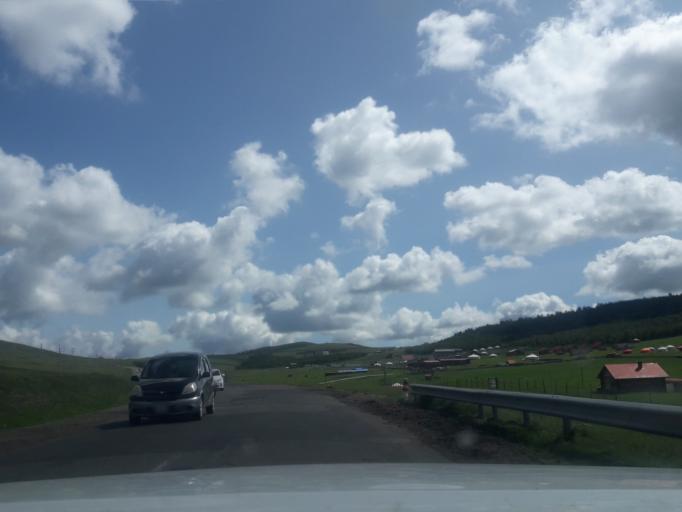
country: MN
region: Central Aimak
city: Ihsueuej
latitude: 48.1467
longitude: 106.4097
